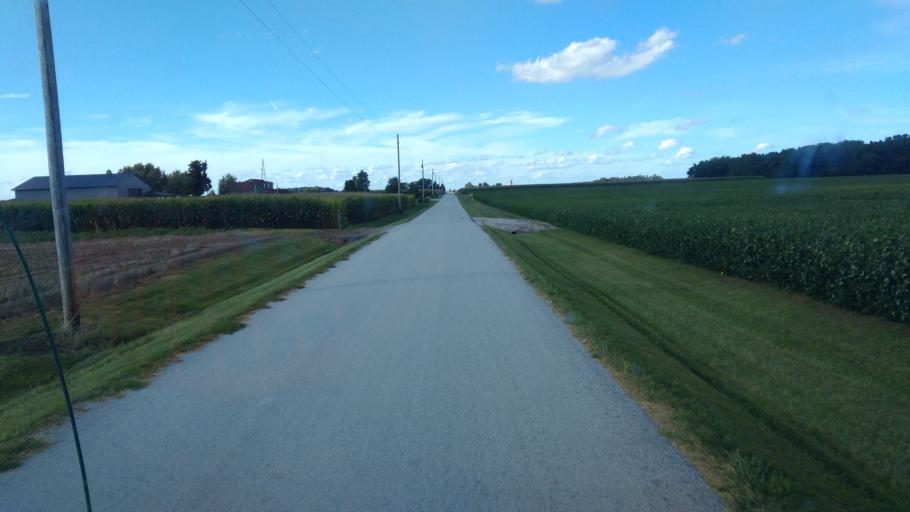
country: US
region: Ohio
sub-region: Hardin County
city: Kenton
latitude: 40.7210
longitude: -83.6724
